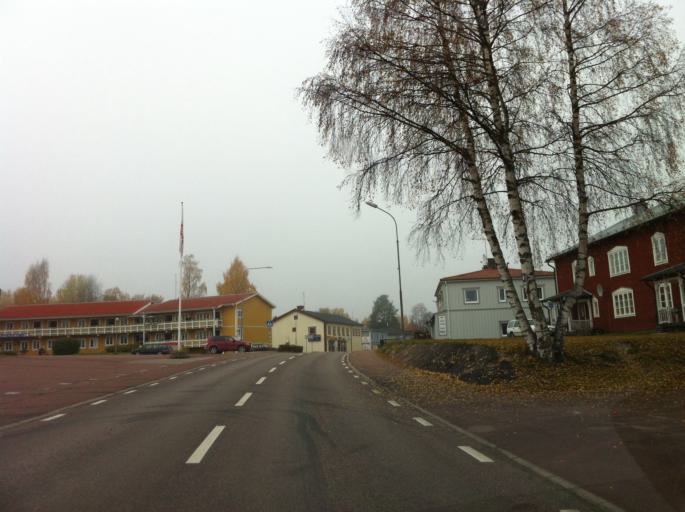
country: NO
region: Hedmark
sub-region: Trysil
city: Innbygda
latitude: 61.6934
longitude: 13.1395
